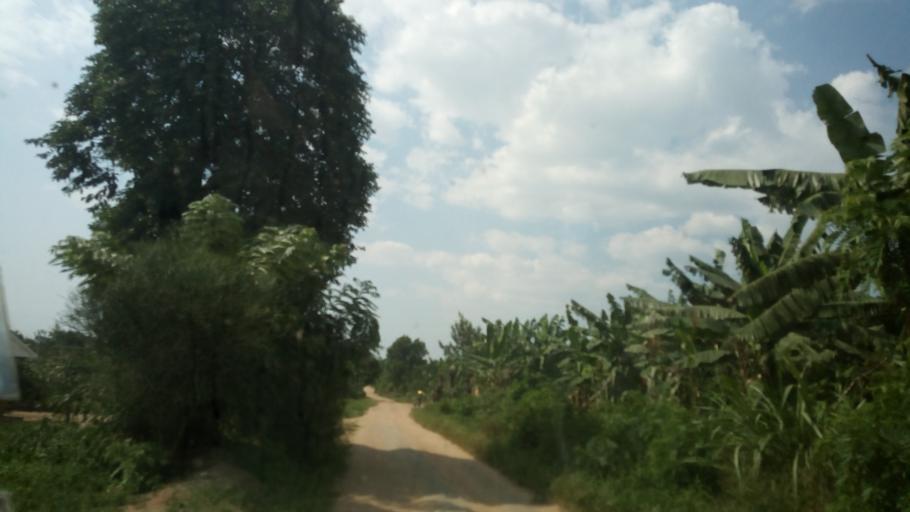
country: UG
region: Western Region
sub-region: Kanungu District
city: Ntungamo
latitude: -0.7852
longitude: 29.6896
